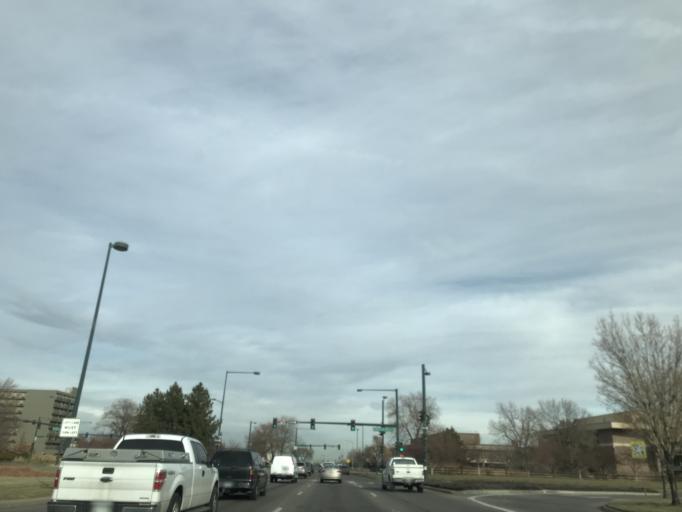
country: US
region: Colorado
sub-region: Adams County
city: Commerce City
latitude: 39.7605
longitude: -104.9028
